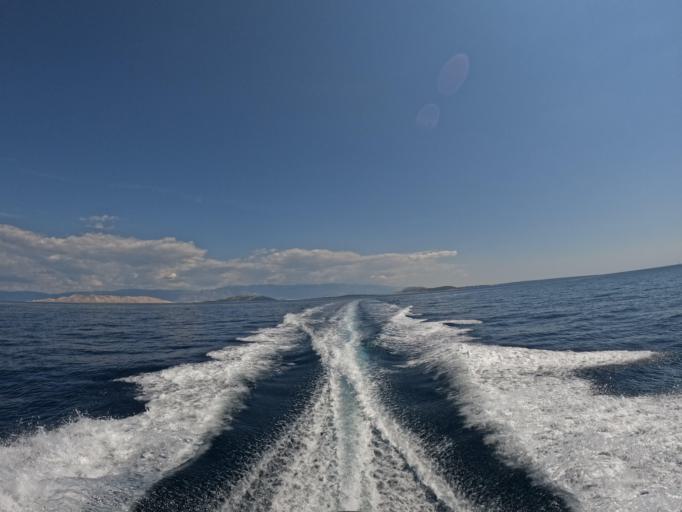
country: HR
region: Primorsko-Goranska
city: Lopar
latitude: 44.8919
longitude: 14.6311
